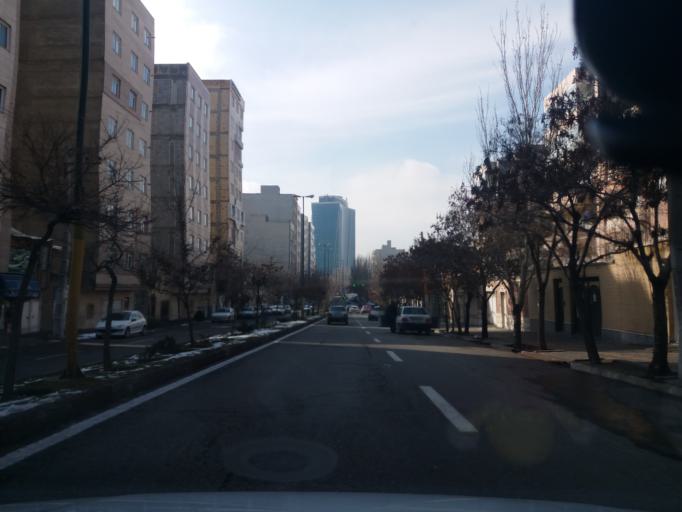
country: IR
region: East Azerbaijan
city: Tabriz
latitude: 38.0369
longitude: 46.3675
